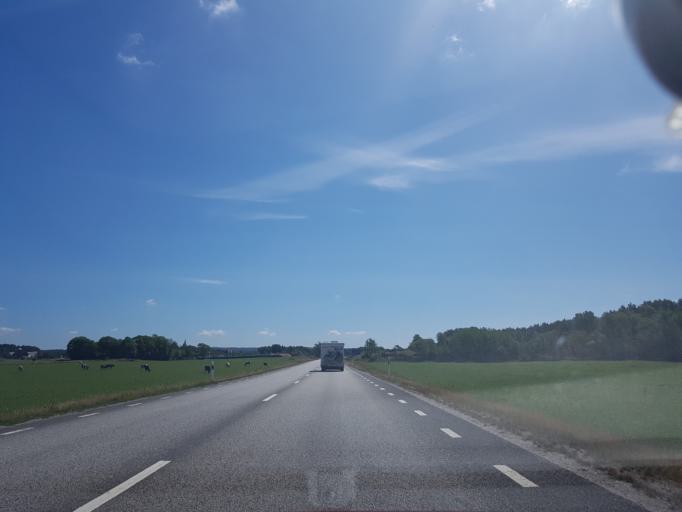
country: SE
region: Vaestra Goetaland
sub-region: Orust
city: Henan
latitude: 58.1515
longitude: 11.5792
